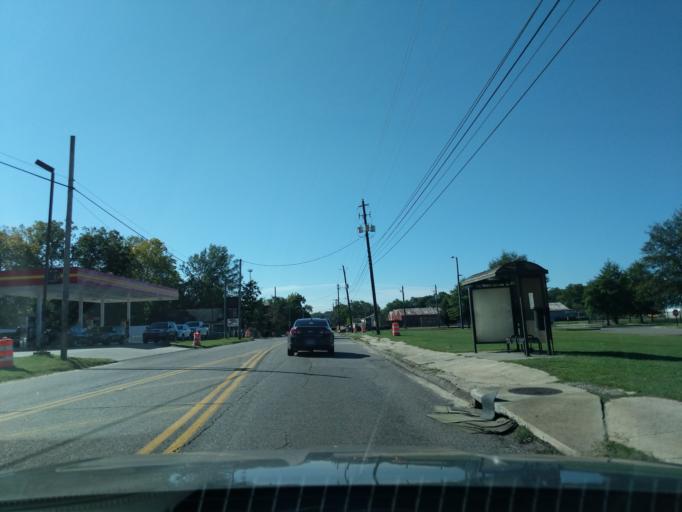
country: US
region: Georgia
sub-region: Richmond County
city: Augusta
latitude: 33.4550
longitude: -81.9991
